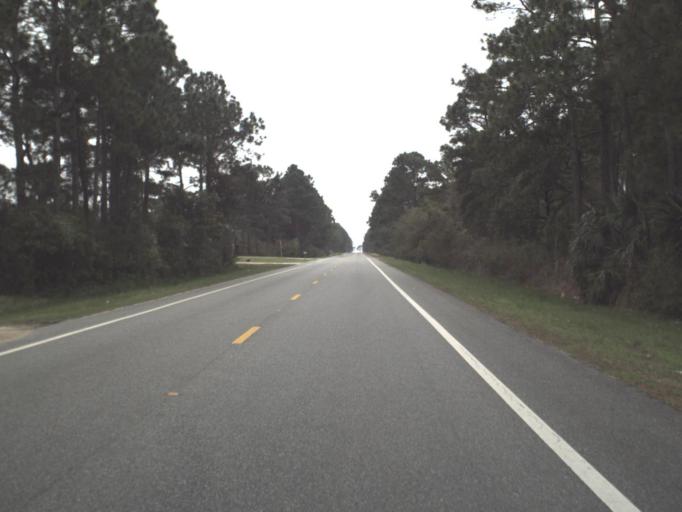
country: US
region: Florida
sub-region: Franklin County
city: Eastpoint
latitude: 29.7751
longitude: -84.8320
